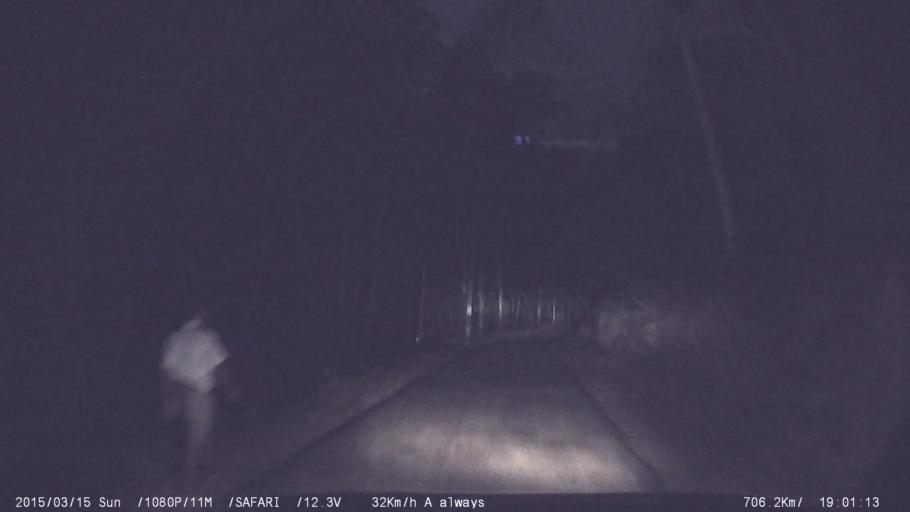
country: IN
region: Kerala
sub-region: Ernakulam
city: Muvattupuzha
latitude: 9.8741
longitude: 76.6539
